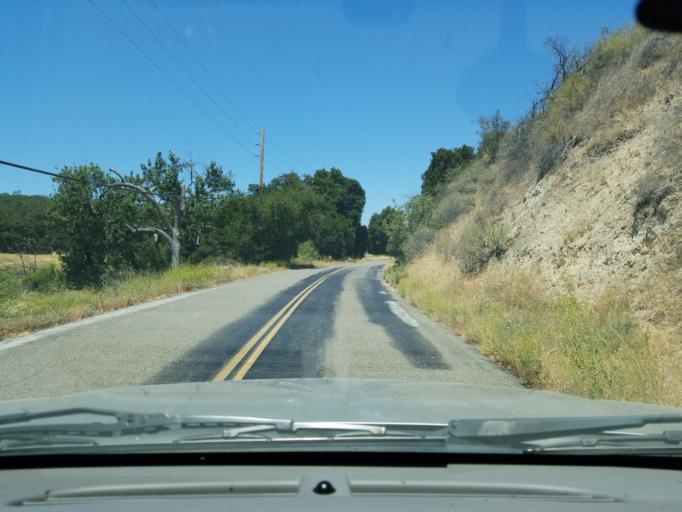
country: US
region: California
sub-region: Monterey County
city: Carmel Valley Village
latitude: 36.4256
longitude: -121.6197
